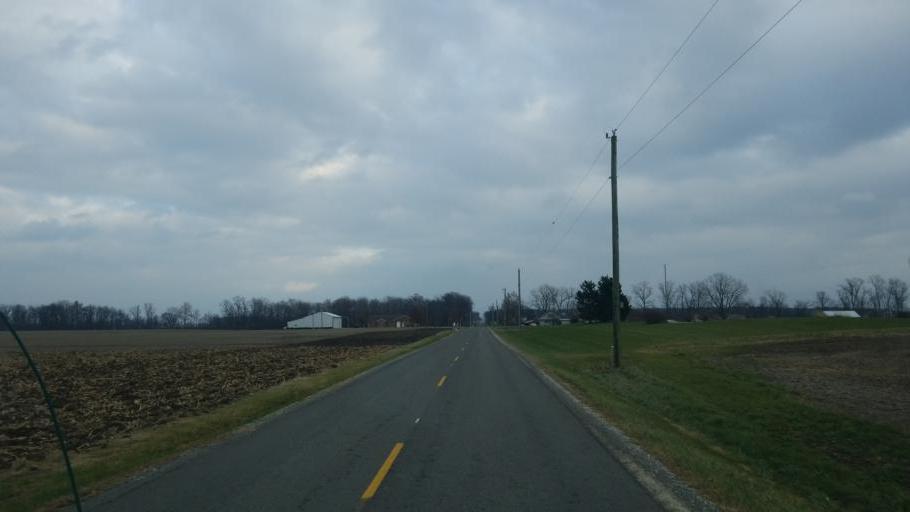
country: US
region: Ohio
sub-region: Mercer County
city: Coldwater
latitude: 40.5090
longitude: -84.6606
